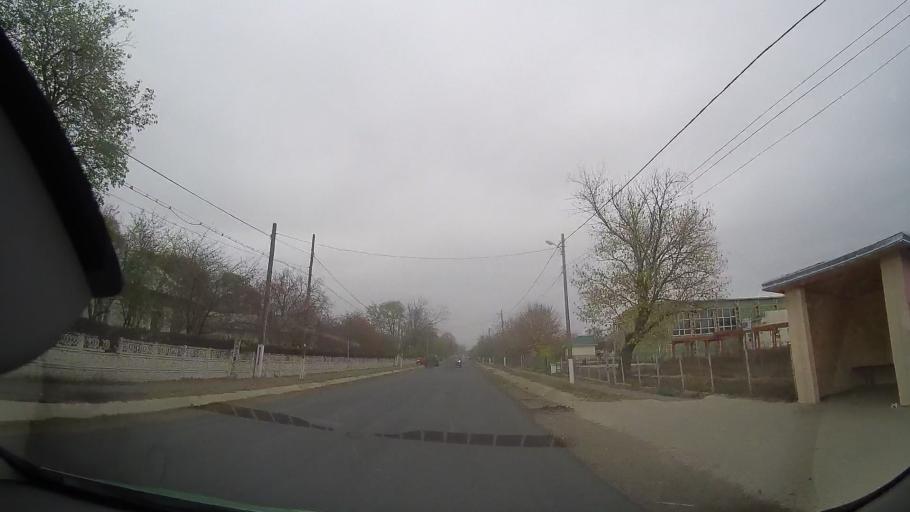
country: RO
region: Braila
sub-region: Comuna Rosiori
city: Rosiori
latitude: 44.8102
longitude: 27.3869
